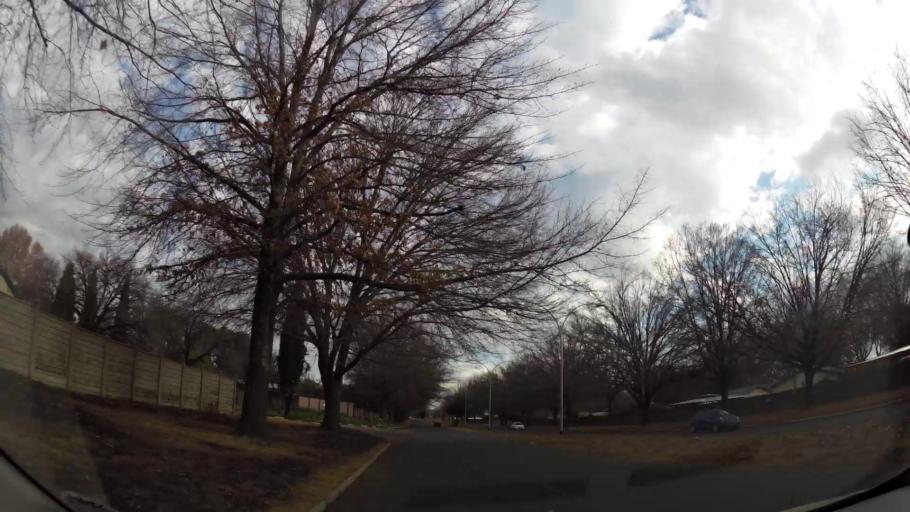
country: ZA
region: Orange Free State
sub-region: Fezile Dabi District Municipality
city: Sasolburg
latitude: -26.8003
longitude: 27.8189
